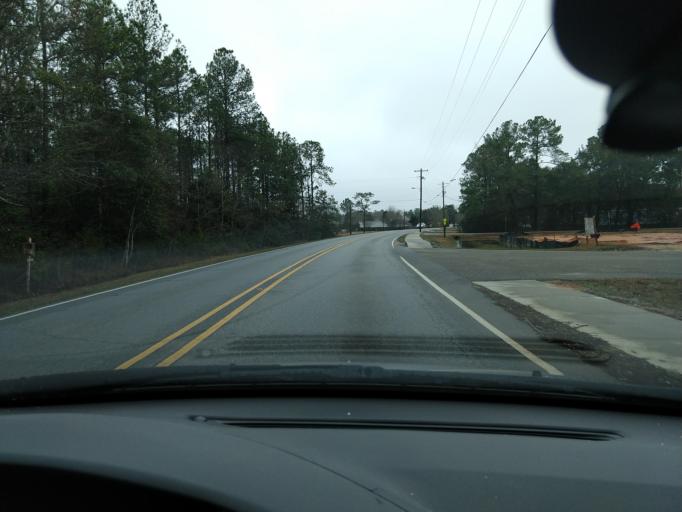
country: US
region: Mississippi
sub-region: Jackson County
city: Gulf Park Estates
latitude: 30.4081
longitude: -88.7831
